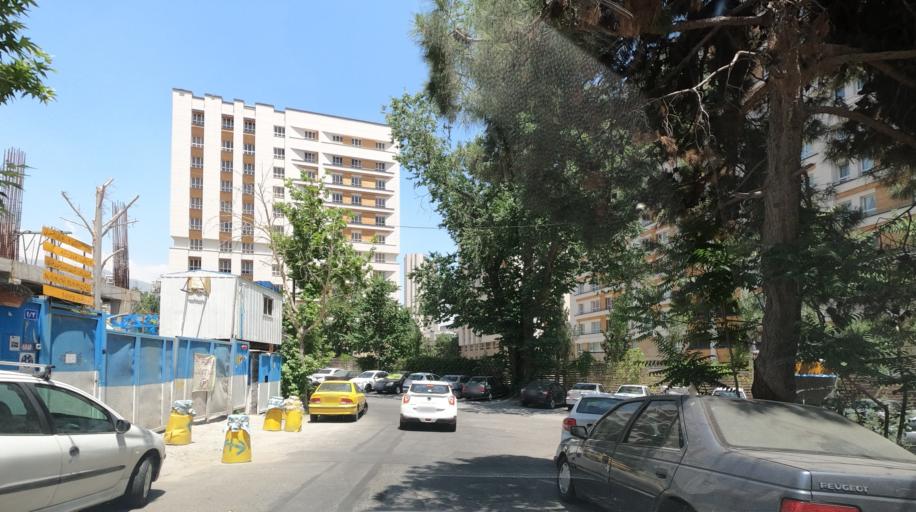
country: IR
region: Tehran
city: Tajrish
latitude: 35.7889
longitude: 51.3851
